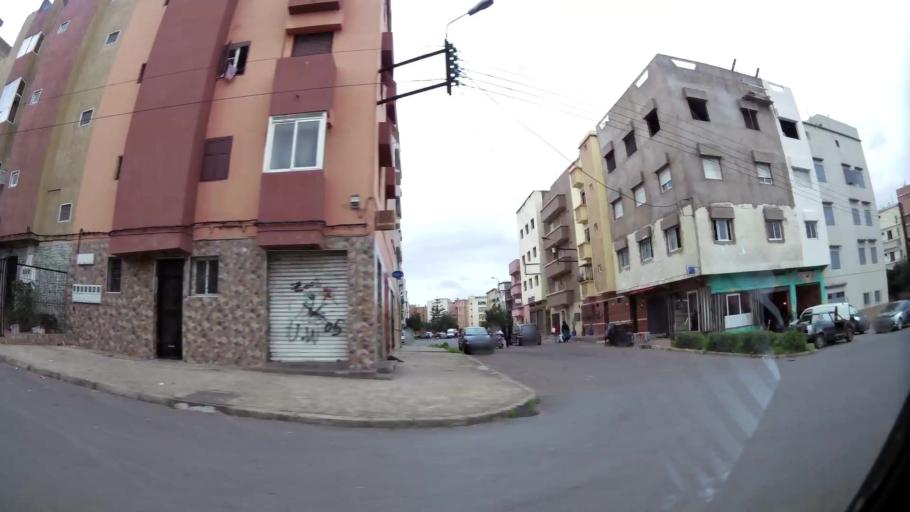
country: MA
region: Grand Casablanca
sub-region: Casablanca
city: Casablanca
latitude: 33.5695
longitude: -7.5544
